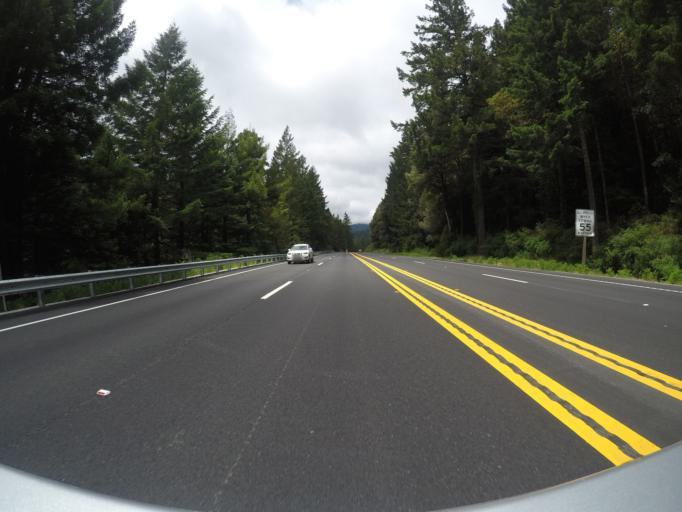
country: US
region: California
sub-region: Humboldt County
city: Redway
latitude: 40.3288
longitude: -123.9243
